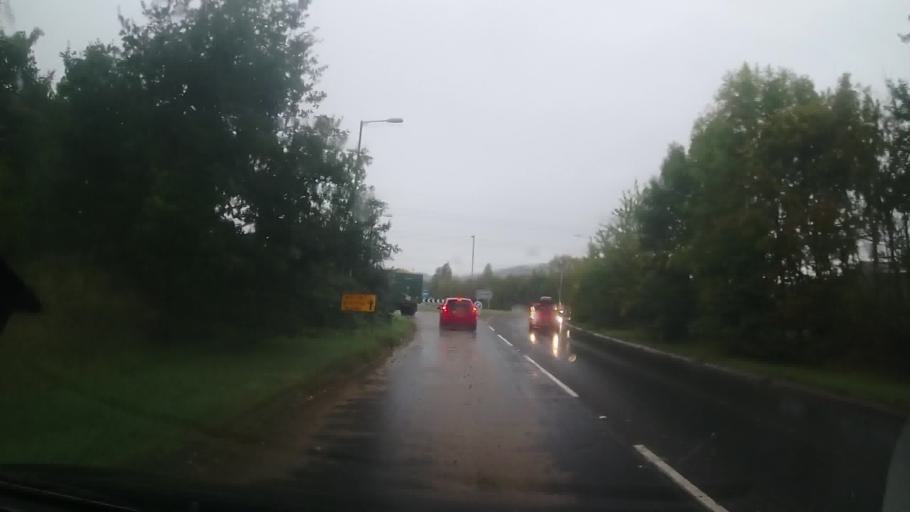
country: GB
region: England
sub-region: Worcestershire
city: Evesham
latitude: 52.1127
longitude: -1.9597
